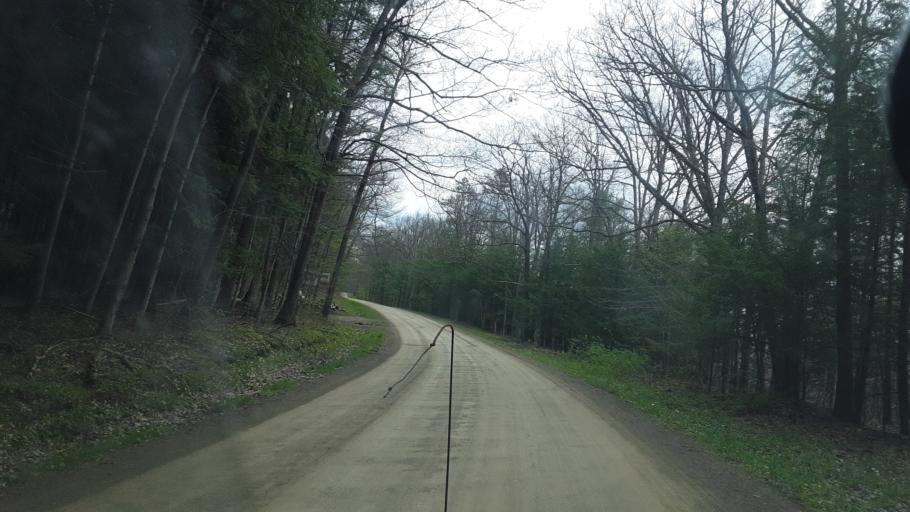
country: US
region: New York
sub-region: Steuben County
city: Addison
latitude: 42.0943
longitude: -77.3264
